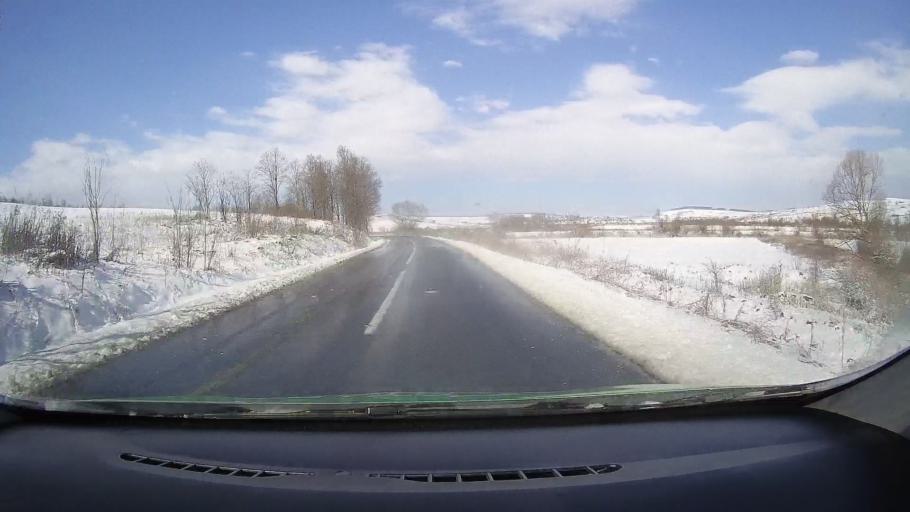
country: RO
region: Sibiu
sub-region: Comuna Nocrich
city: Nocrich
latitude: 45.9073
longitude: 24.4635
